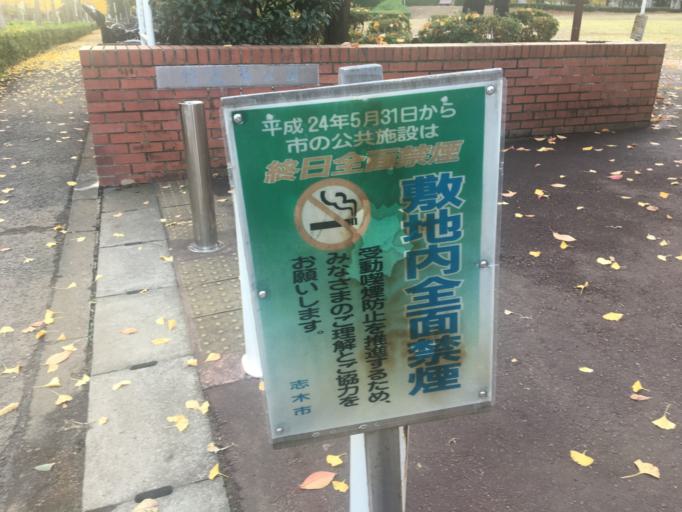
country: JP
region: Saitama
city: Shiki
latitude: 35.8284
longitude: 139.5592
